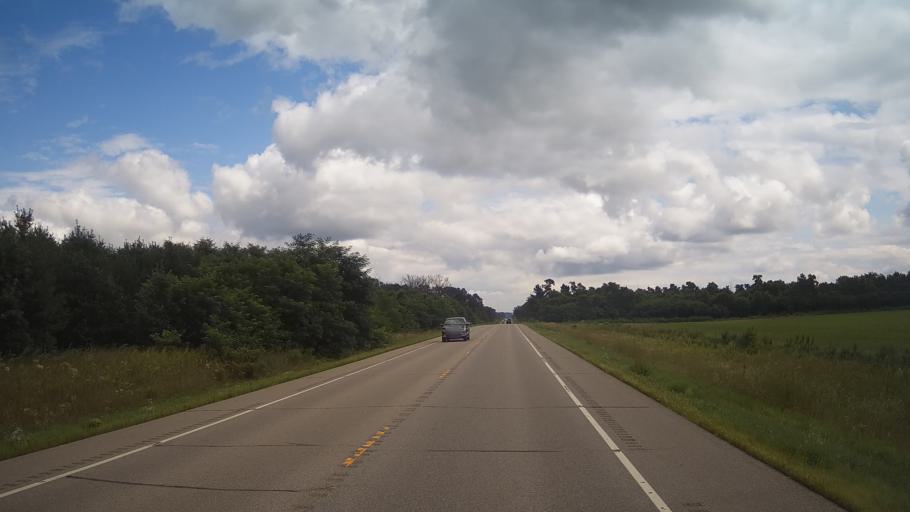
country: US
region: Wisconsin
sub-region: Adams County
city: Friendship
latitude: 44.0219
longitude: -89.6520
